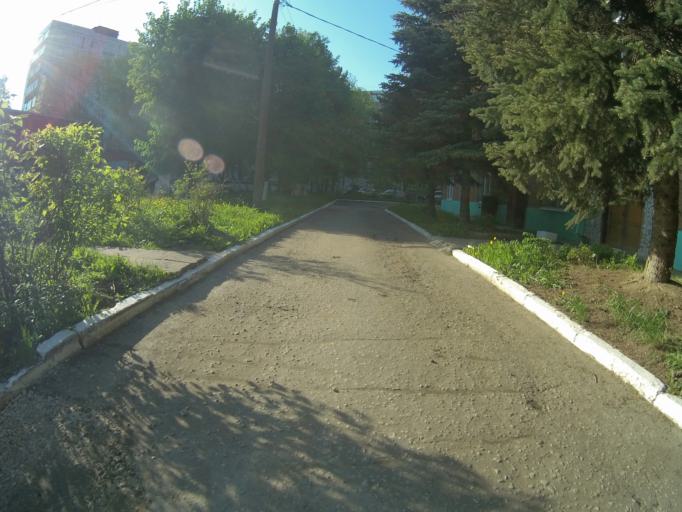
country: RU
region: Vladimir
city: Kommunar
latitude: 56.1720
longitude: 40.4547
